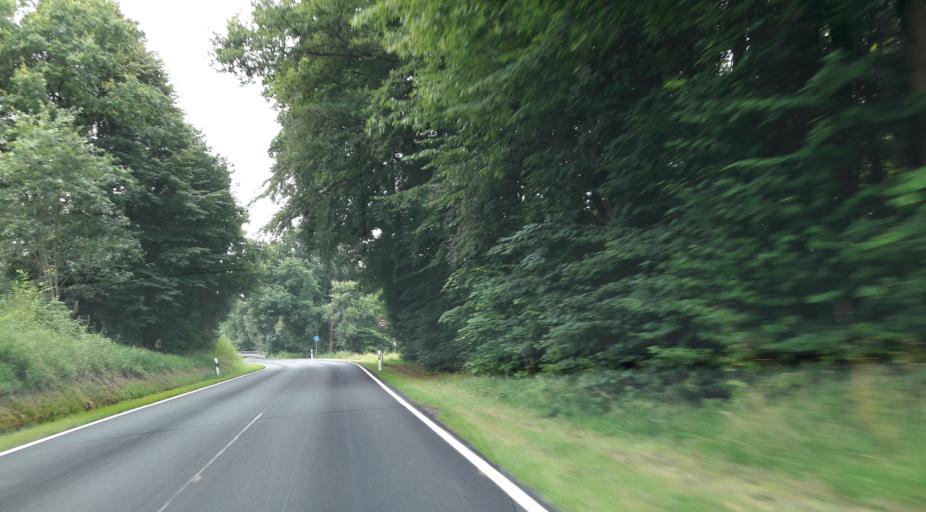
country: DE
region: Rheinland-Pfalz
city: Waldmohr
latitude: 49.3789
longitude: 7.3186
